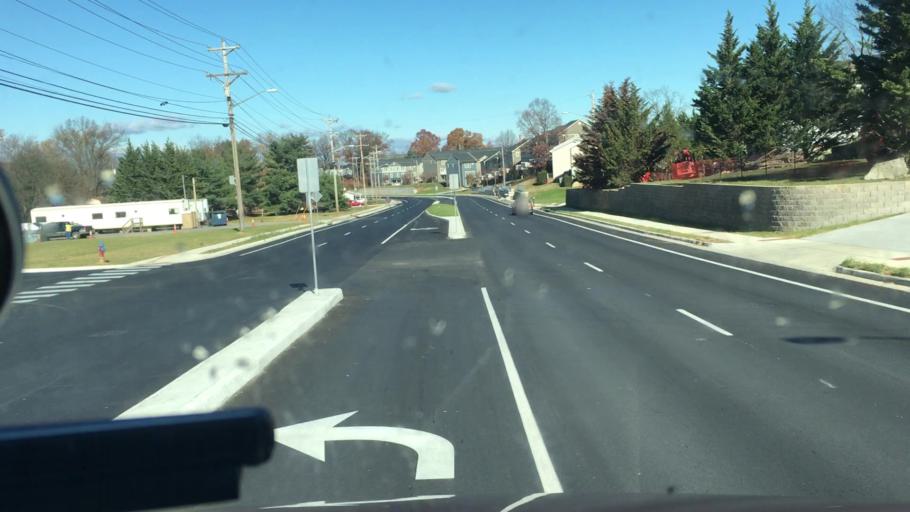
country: US
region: Virginia
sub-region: Rockingham County
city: Massanetta Springs
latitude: 38.4198
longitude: -78.8541
